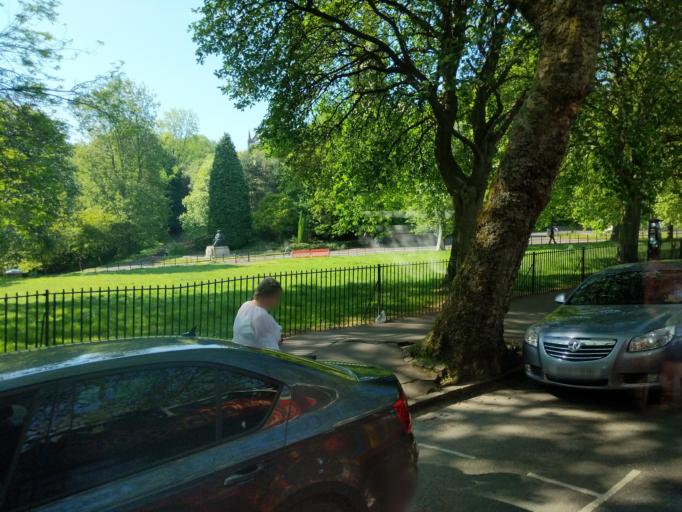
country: GB
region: Scotland
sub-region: Glasgow City
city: Glasgow
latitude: 55.8690
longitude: -4.2871
